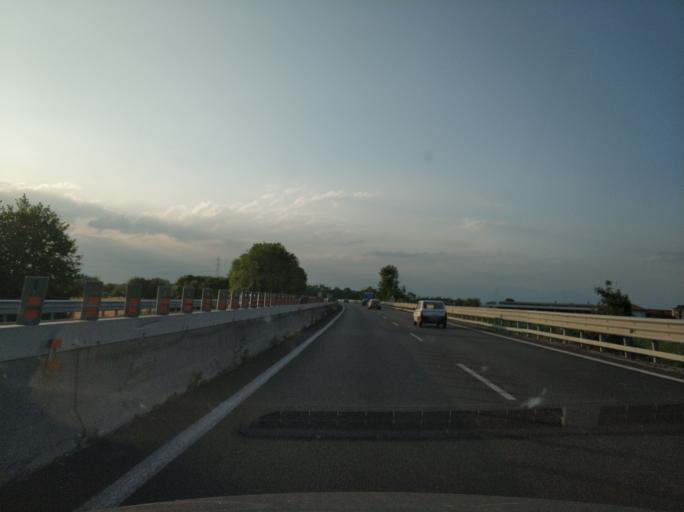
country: IT
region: Piedmont
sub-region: Provincia di Torino
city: Borgaro Torinese
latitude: 45.1602
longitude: 7.6852
